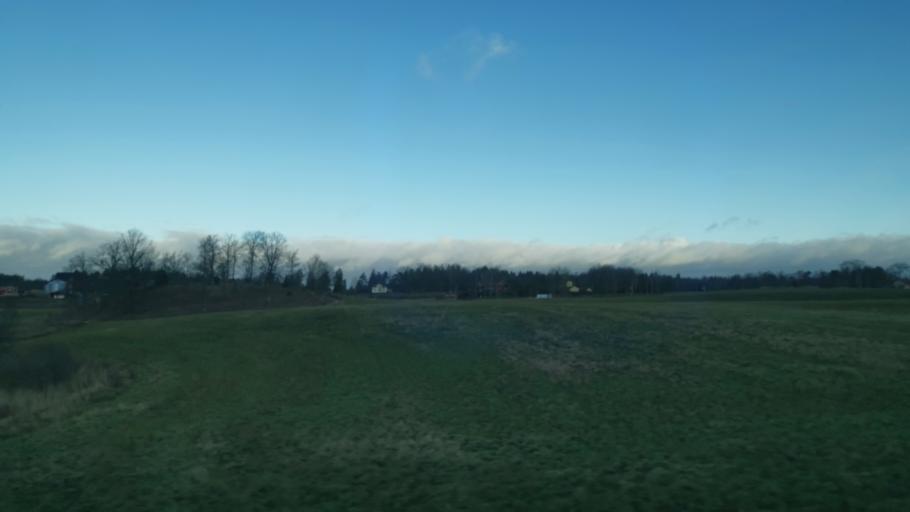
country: SE
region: Soedermanland
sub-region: Flens Kommun
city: Malmkoping
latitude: 59.0684
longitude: 16.8089
